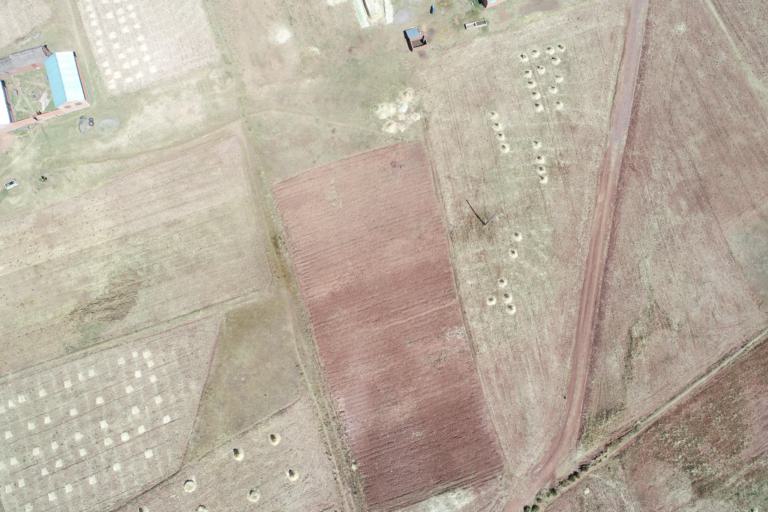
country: BO
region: La Paz
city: Tiahuanaco
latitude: -16.5883
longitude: -68.7697
